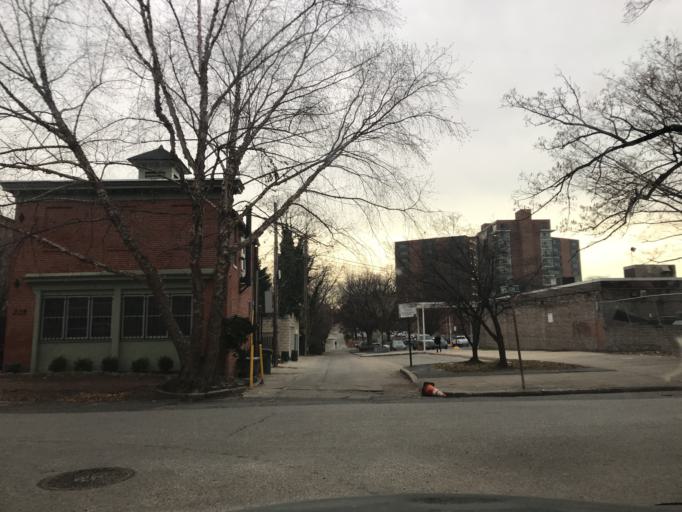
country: US
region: Maryland
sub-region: City of Baltimore
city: Baltimore
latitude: 39.3082
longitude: -76.6285
